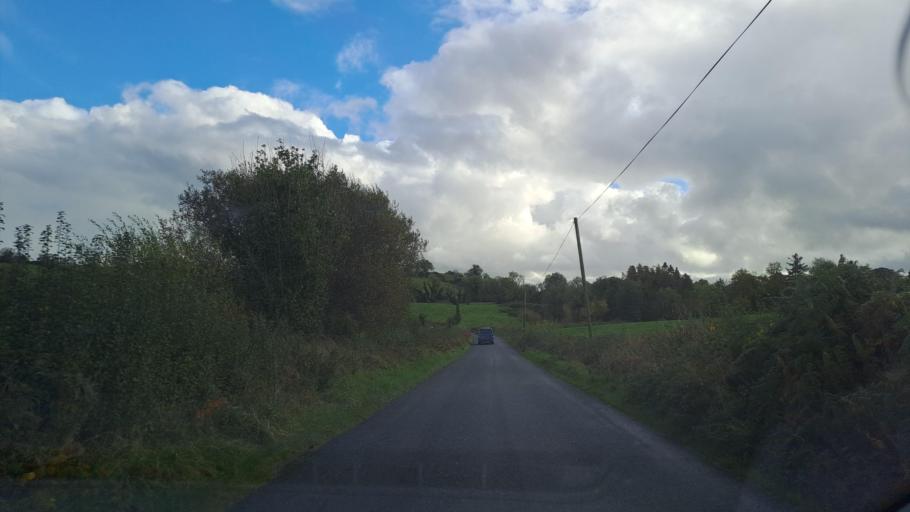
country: IE
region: Ulster
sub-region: An Cabhan
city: Bailieborough
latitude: 53.9957
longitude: -6.9674
